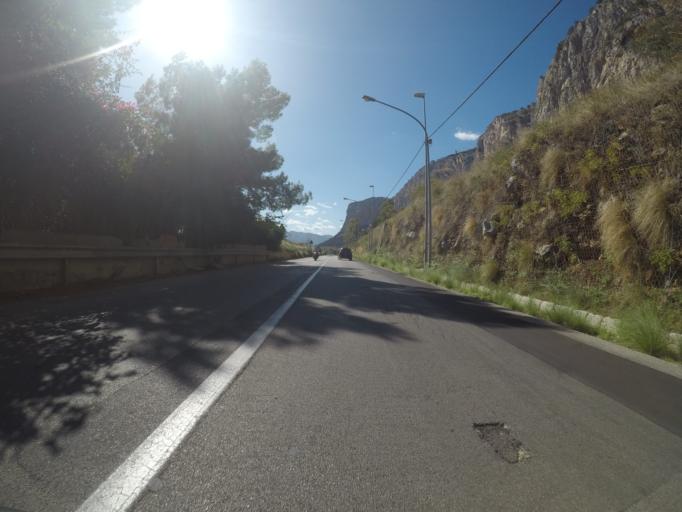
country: IT
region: Sicily
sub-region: Palermo
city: Palermo
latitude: 38.1760
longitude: 13.3660
